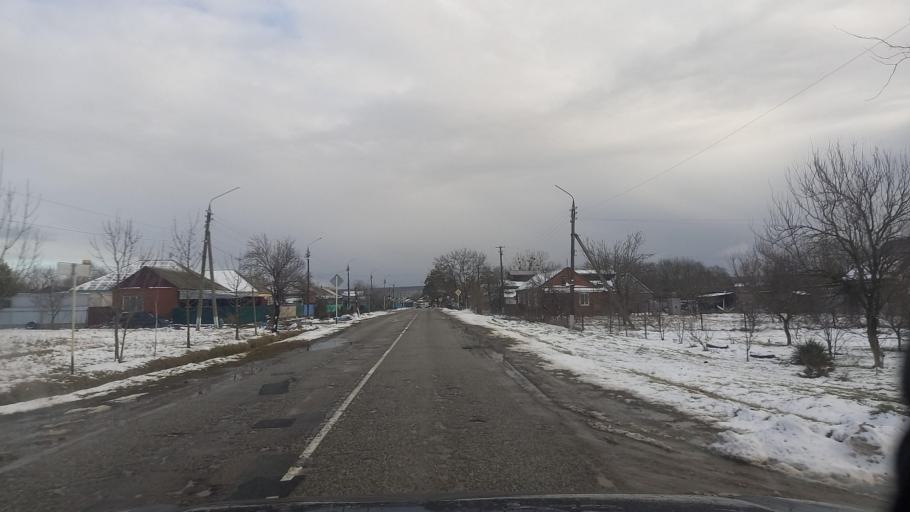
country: RU
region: Krasnodarskiy
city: Smolenskaya
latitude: 44.7768
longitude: 38.8344
